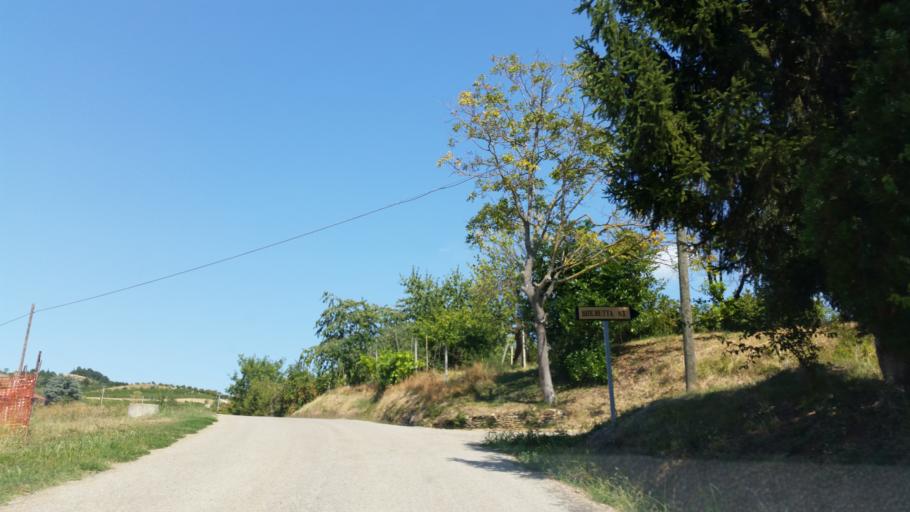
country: IT
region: Piedmont
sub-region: Provincia di Cuneo
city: Sinio
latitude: 44.5994
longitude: 8.0279
